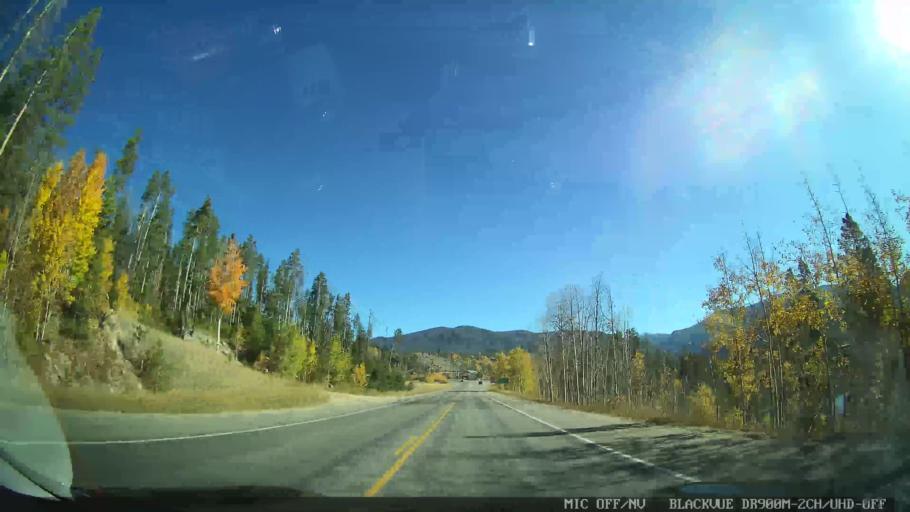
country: US
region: Colorado
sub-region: Grand County
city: Granby
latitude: 40.2479
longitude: -105.8389
